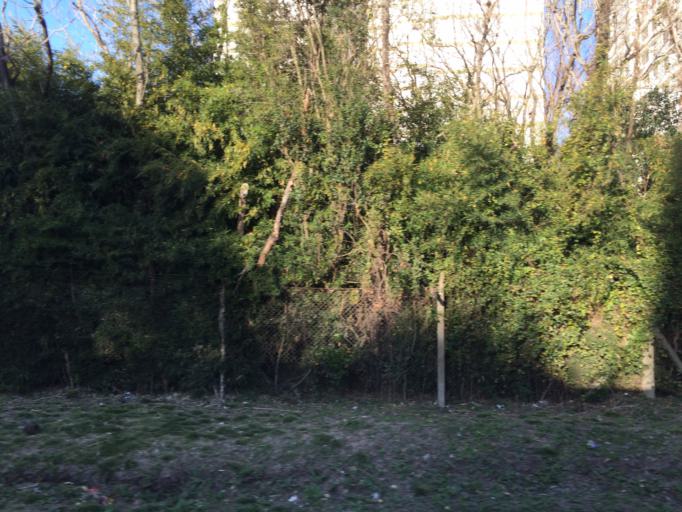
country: AR
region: Buenos Aires
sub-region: Partido de Lomas de Zamora
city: Lomas de Zamora
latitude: -34.7737
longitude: -58.3965
